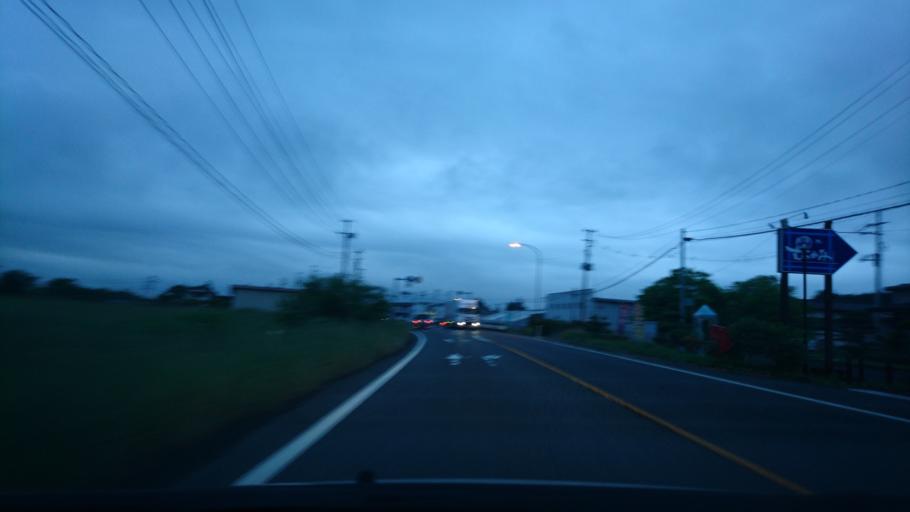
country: JP
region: Iwate
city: Ichinoseki
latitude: 38.8177
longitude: 141.0768
